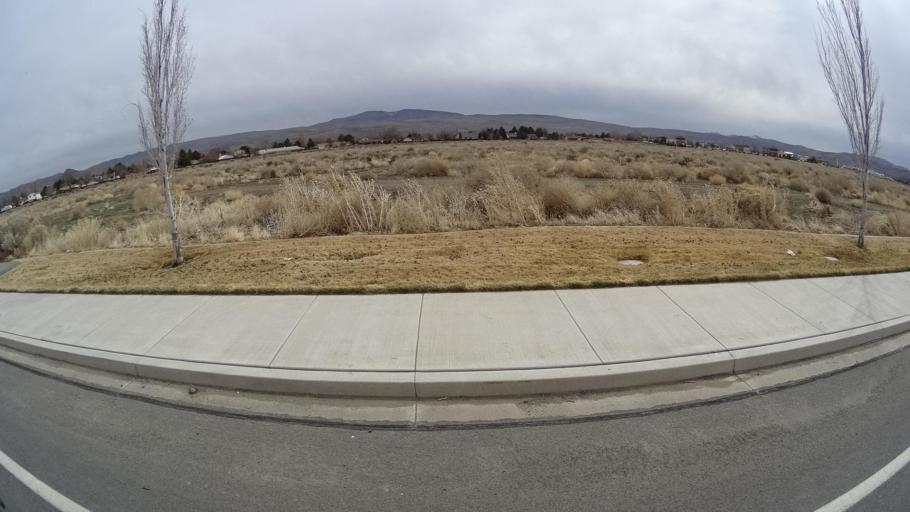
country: US
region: Nevada
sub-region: Washoe County
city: Spanish Springs
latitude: 39.6431
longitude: -119.7175
